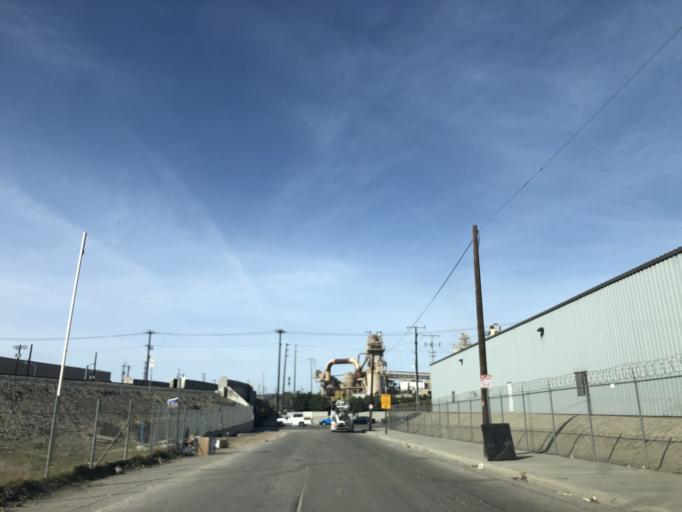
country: US
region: California
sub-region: Los Angeles County
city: North Hollywood
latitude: 34.2270
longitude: -118.3796
